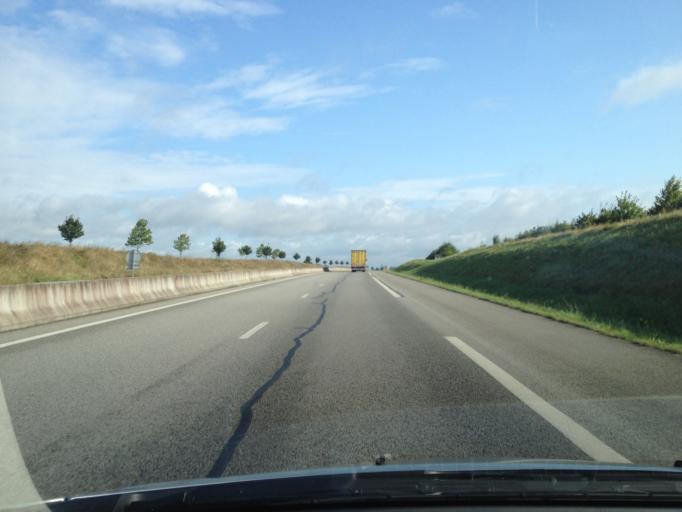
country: FR
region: Lower Normandy
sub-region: Departement de l'Orne
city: Sees
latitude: 48.5659
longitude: 0.1753
